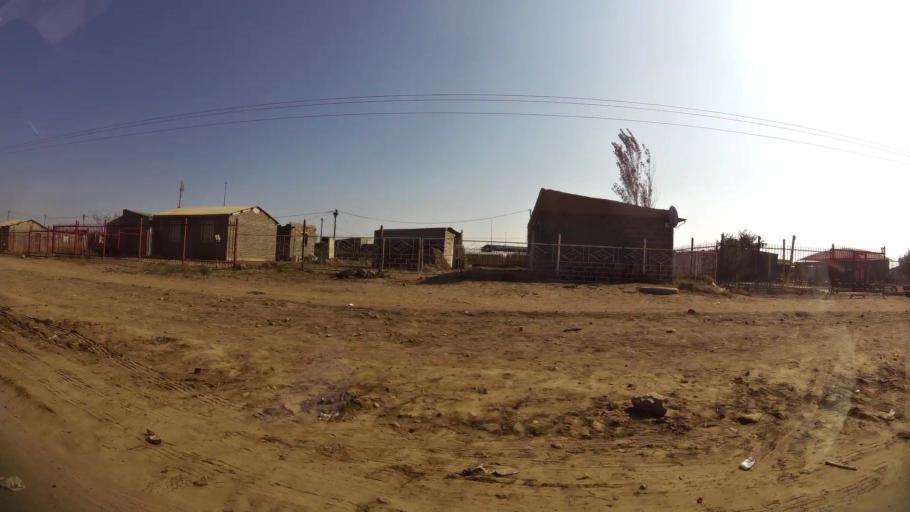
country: ZA
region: Orange Free State
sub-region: Mangaung Metropolitan Municipality
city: Bloemfontein
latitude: -29.1931
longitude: 26.2813
